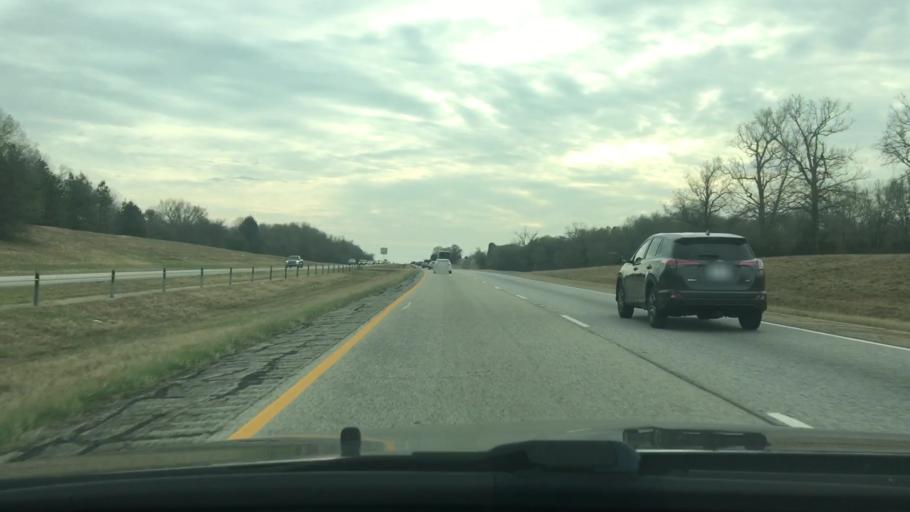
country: US
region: Texas
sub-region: Leon County
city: Centerville
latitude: 31.2324
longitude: -95.9943
